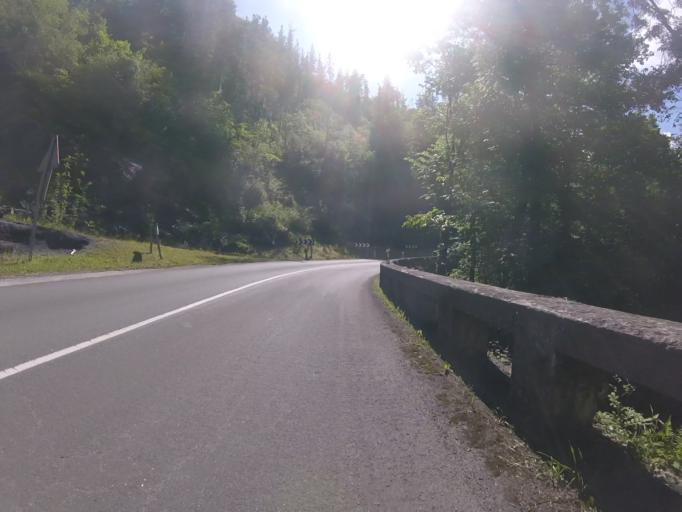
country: ES
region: Basque Country
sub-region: Provincia de Guipuzcoa
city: Azpeitia
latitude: 43.1766
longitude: -2.2227
